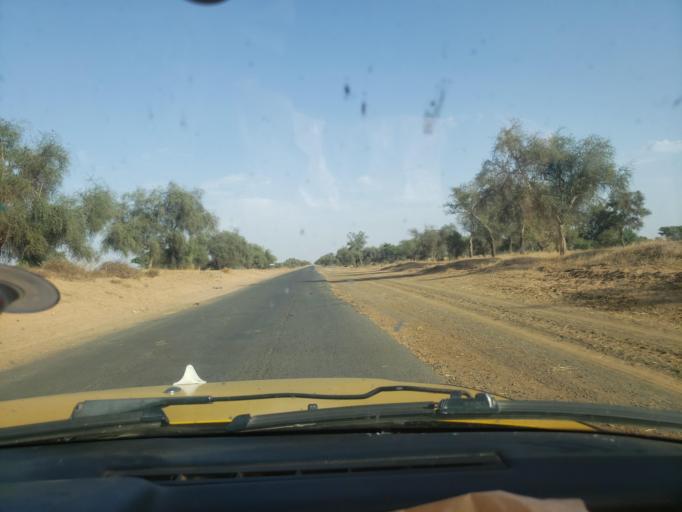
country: SN
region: Louga
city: Louga
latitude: 15.5074
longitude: -15.9692
